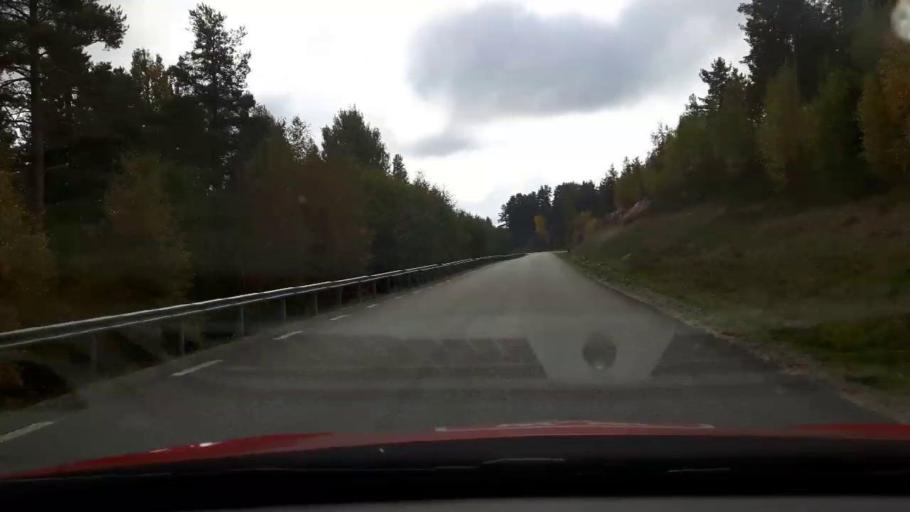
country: SE
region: Gaevleborg
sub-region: Ljusdals Kommun
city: Farila
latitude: 61.7949
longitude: 15.9131
